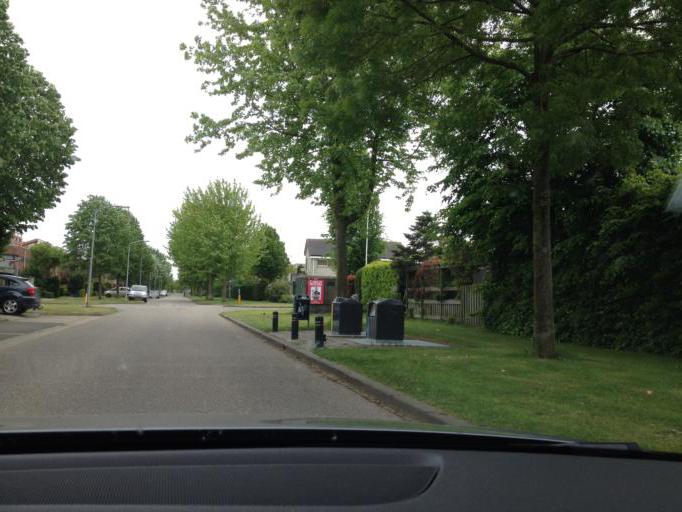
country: NL
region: Flevoland
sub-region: Gemeente Almere
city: Almere Stad
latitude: 52.3653
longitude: 5.2370
